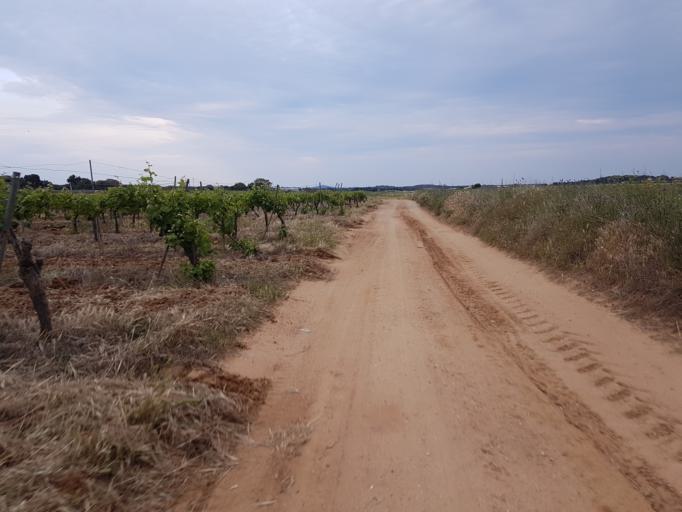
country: FR
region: Languedoc-Roussillon
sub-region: Departement de l'Herault
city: Portiragnes
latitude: 43.3181
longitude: 3.3230
